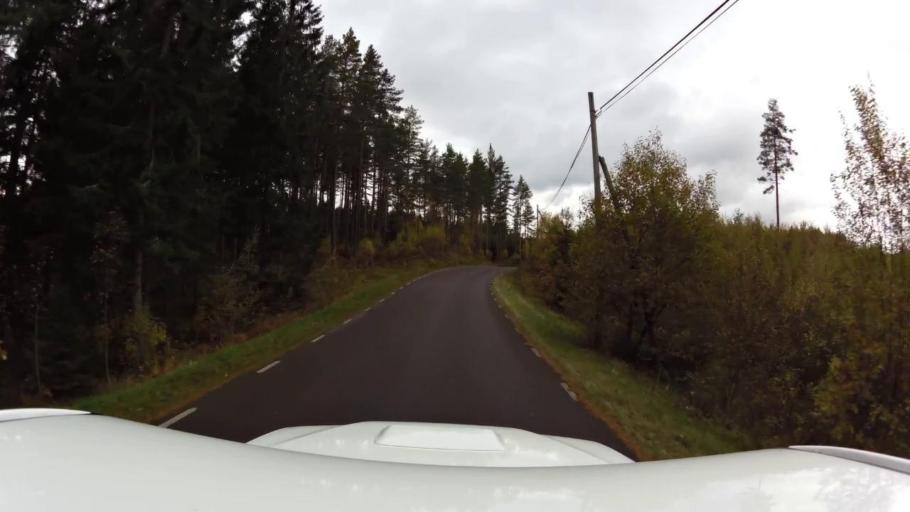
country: SE
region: OEstergoetland
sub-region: Motala Kommun
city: Borensberg
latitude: 58.5610
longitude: 15.3925
